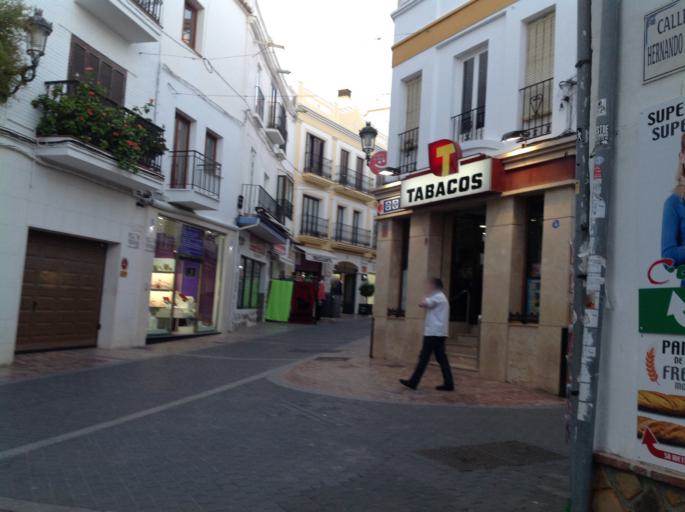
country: ES
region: Andalusia
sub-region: Provincia de Malaga
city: Nerja
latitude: 36.7457
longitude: -3.8758
